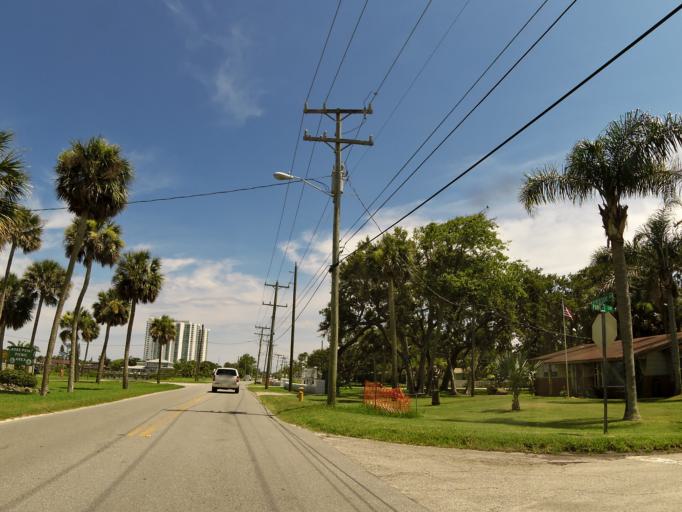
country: US
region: Florida
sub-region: Volusia County
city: Holly Hill
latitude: 29.2382
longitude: -81.0324
